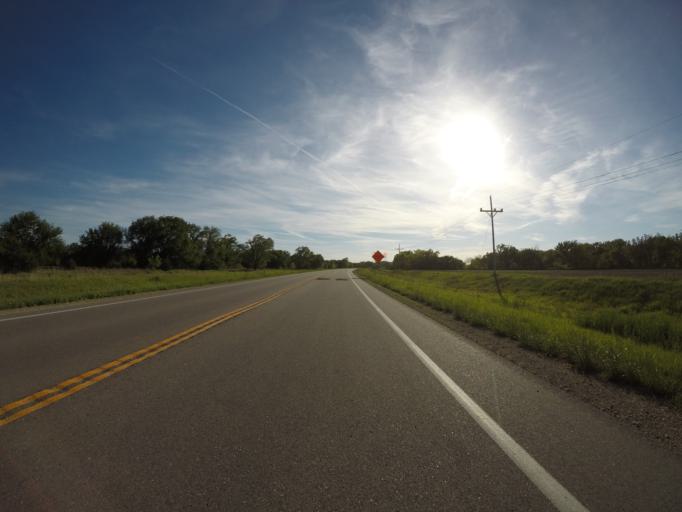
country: US
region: Kansas
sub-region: Cloud County
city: Concordia
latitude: 39.5720
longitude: -97.4319
